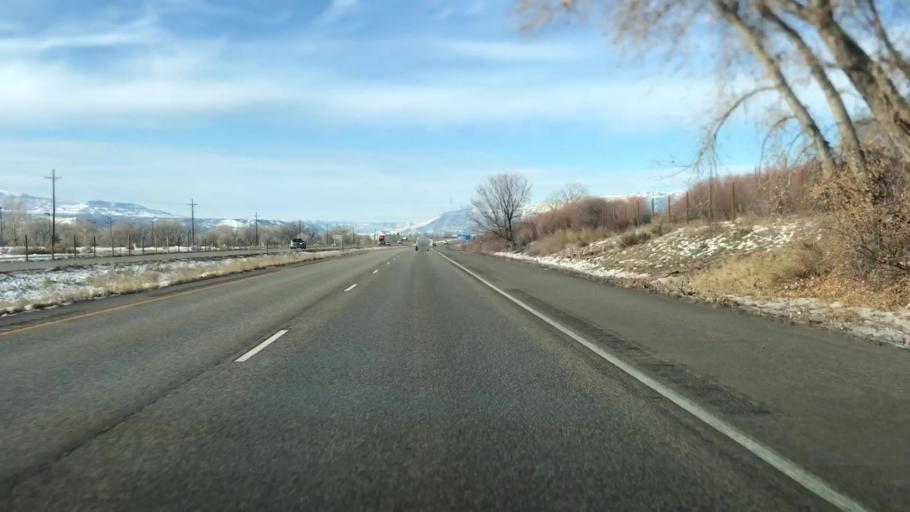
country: US
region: Colorado
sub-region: Garfield County
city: Silt
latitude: 39.5446
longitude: -107.6358
